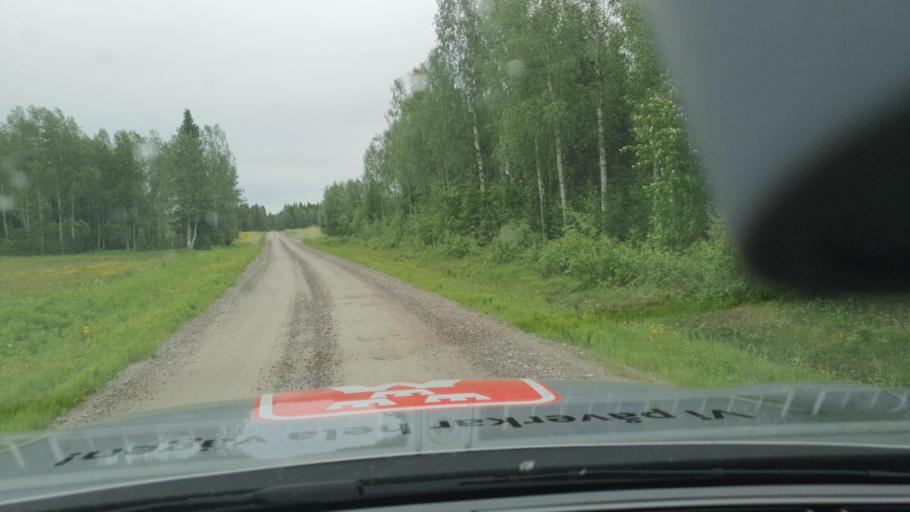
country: SE
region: Norrbotten
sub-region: Overkalix Kommun
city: OEverkalix
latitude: 66.0820
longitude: 22.9030
